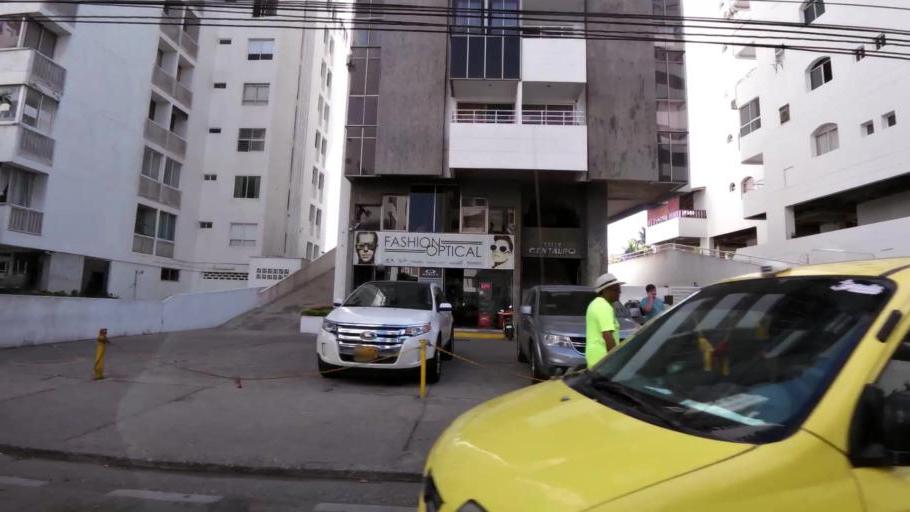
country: CO
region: Bolivar
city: Cartagena
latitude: 10.3941
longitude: -75.5612
